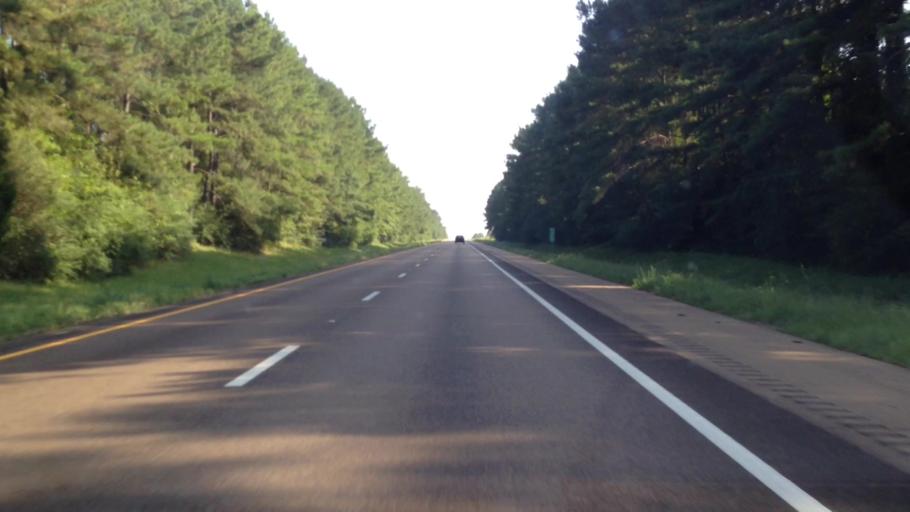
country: US
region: Mississippi
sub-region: Pike County
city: Summit
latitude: 31.3612
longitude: -90.4791
